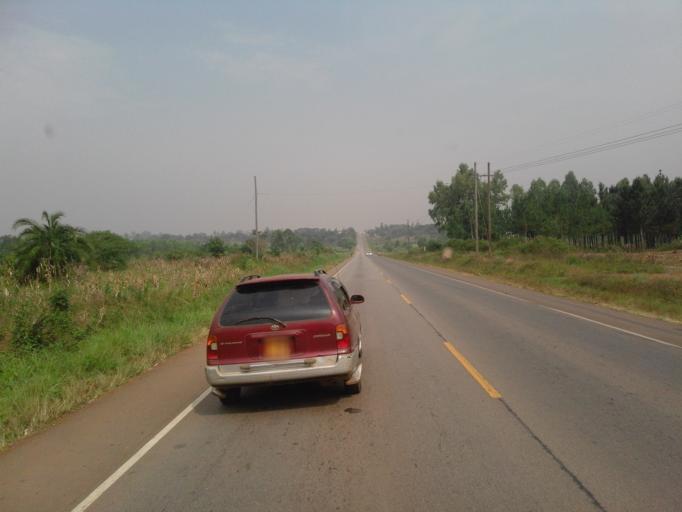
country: UG
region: Eastern Region
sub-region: Bugiri District
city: Bugiri
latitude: 0.5449
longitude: 33.7741
